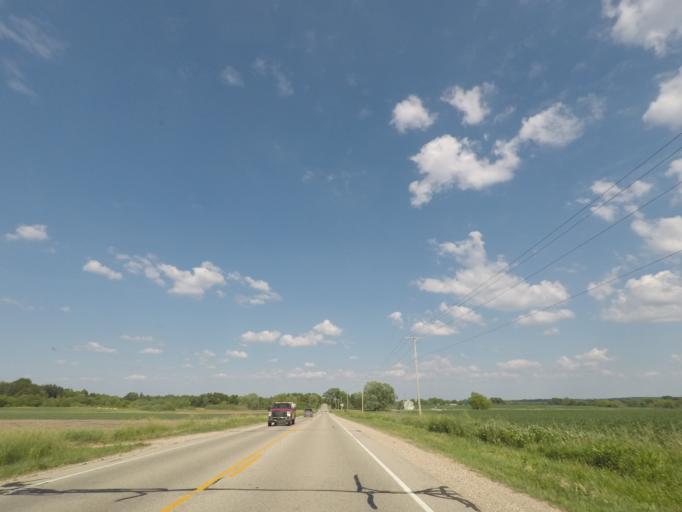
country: US
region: Wisconsin
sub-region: Walworth County
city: East Troy
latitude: 42.7930
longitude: -88.4840
